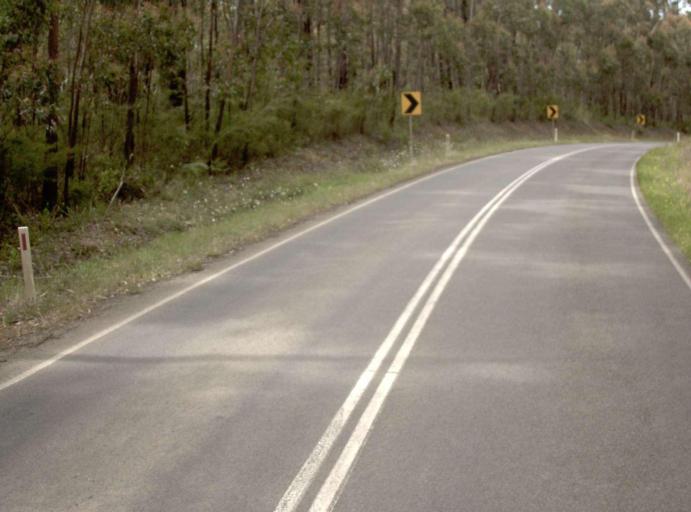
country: AU
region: Victoria
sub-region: Latrobe
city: Traralgon
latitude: -38.0159
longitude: 146.4210
